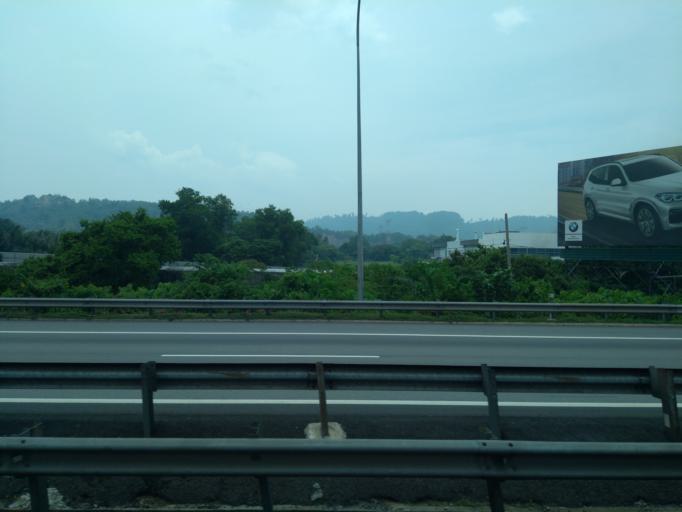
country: MY
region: Penang
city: Juru
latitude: 5.3316
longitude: 100.4356
